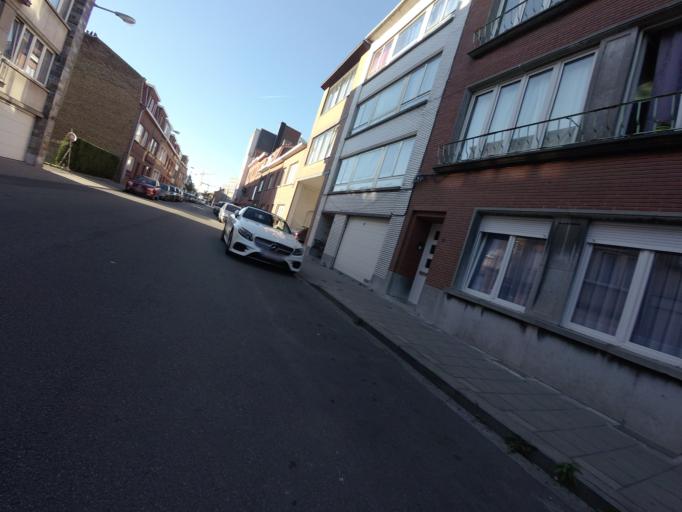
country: BE
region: Flanders
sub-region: Provincie Vlaams-Brabant
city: Diegem
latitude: 50.8594
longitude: 4.4195
